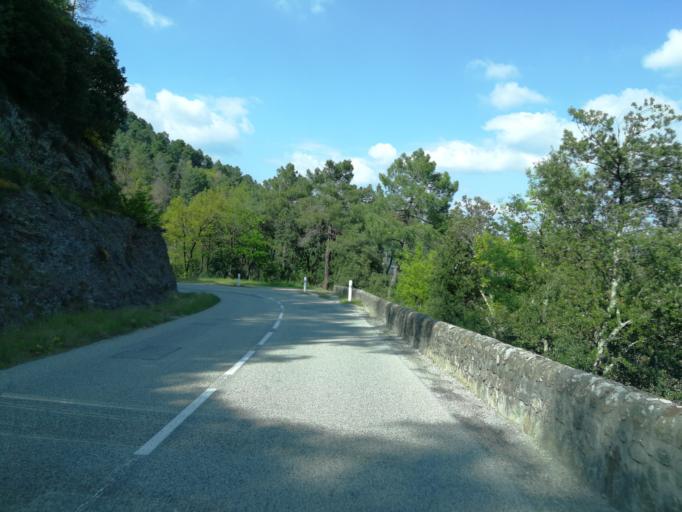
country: FR
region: Rhone-Alpes
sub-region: Departement de l'Ardeche
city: Saint-Sauveur-de-Montagut
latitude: 44.7925
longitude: 4.6130
